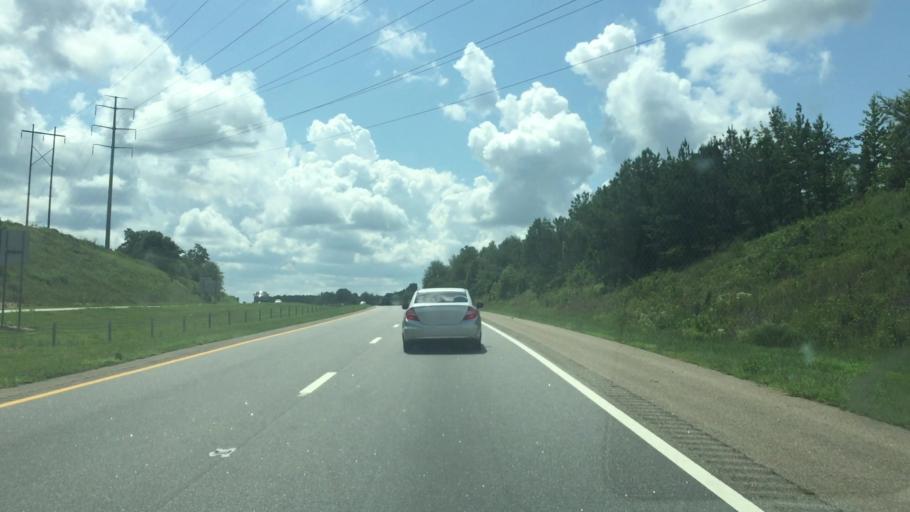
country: US
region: North Carolina
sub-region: Richmond County
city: Cordova
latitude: 34.9386
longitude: -79.8417
